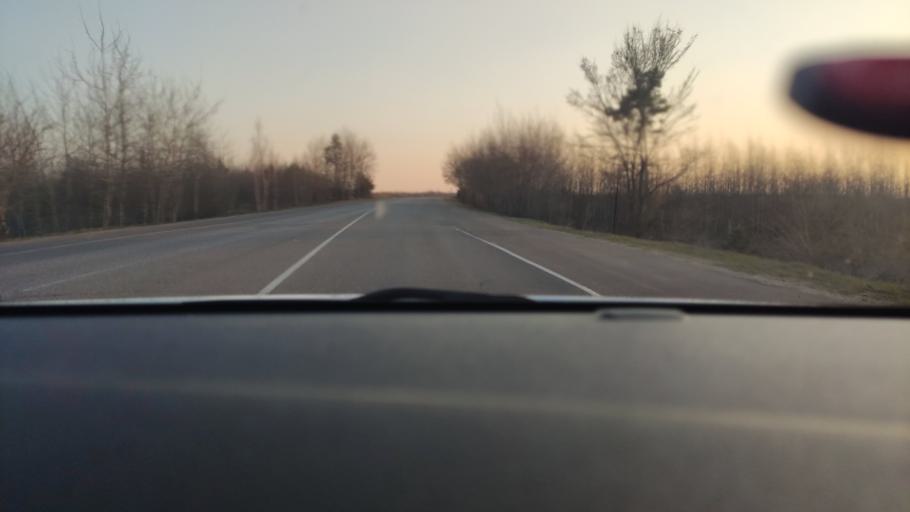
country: RU
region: Voronezj
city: Kolodeznyy
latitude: 51.3758
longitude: 39.2122
